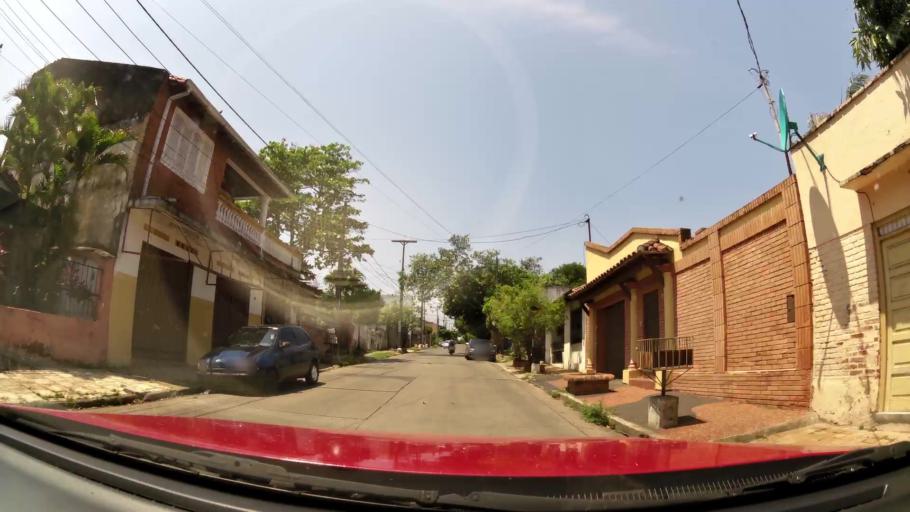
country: PY
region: Asuncion
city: Asuncion
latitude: -25.2985
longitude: -57.6521
